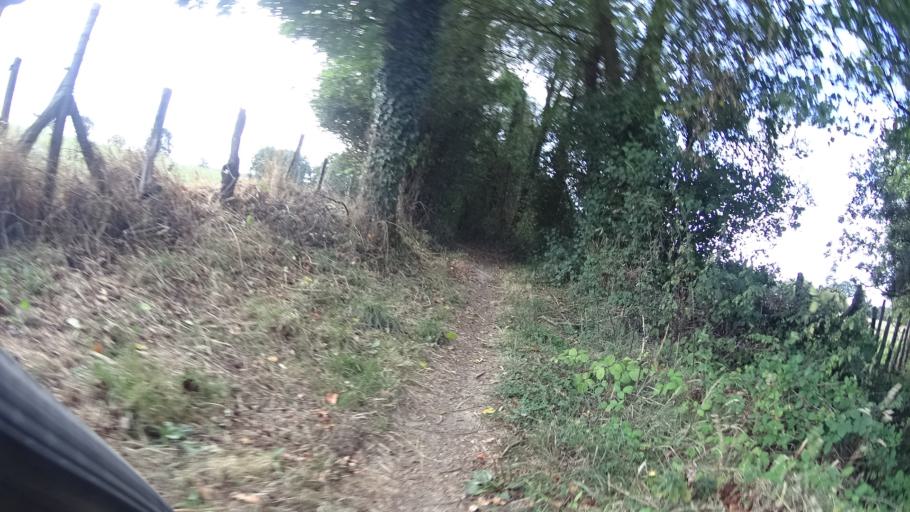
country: FR
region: Brittany
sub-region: Departement d'Ille-et-Vilaine
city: La Meziere
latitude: 48.2209
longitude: -1.7338
